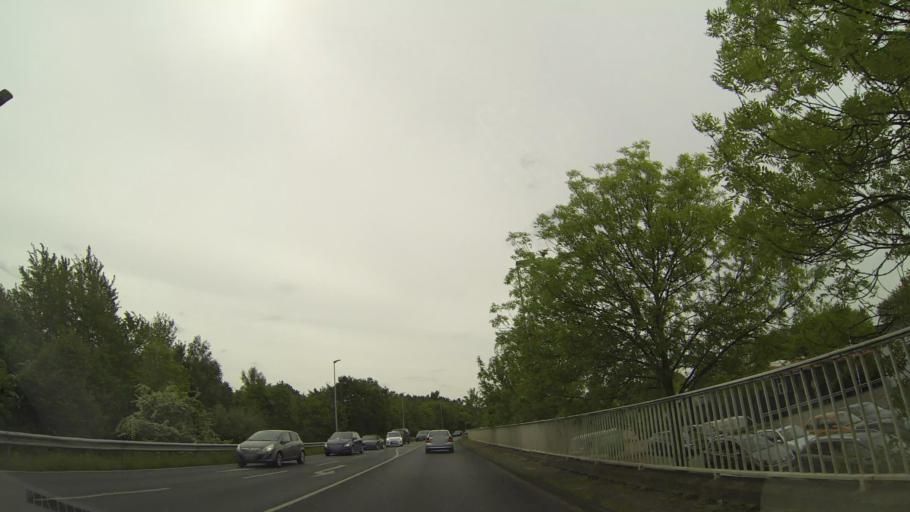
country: DE
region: Schleswig-Holstein
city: Halstenbek
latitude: 53.6273
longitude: 9.8691
